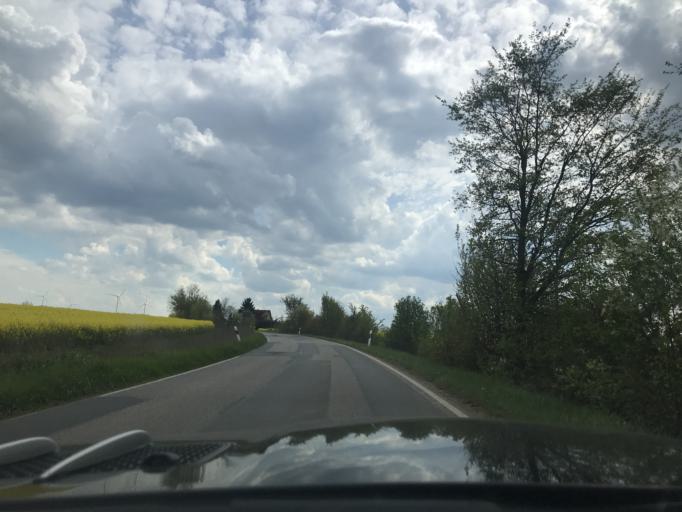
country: DE
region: Schleswig-Holstein
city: Timmendorfer Strand
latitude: 53.9559
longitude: 10.7896
